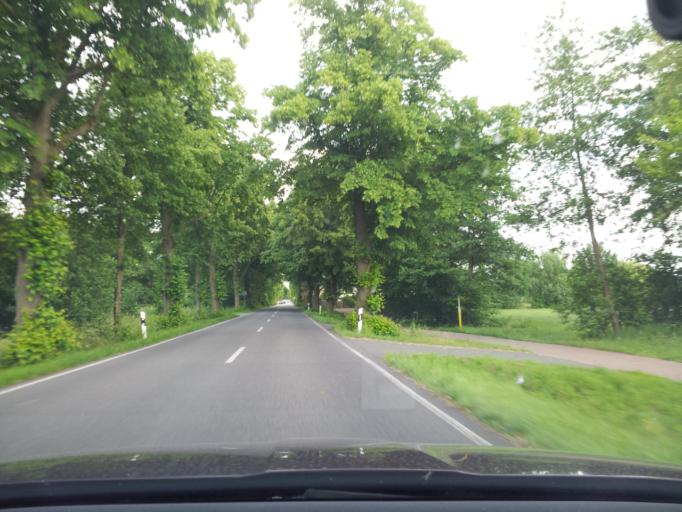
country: DE
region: Brandenburg
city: Juterbog
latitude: 52.0270
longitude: 13.0955
